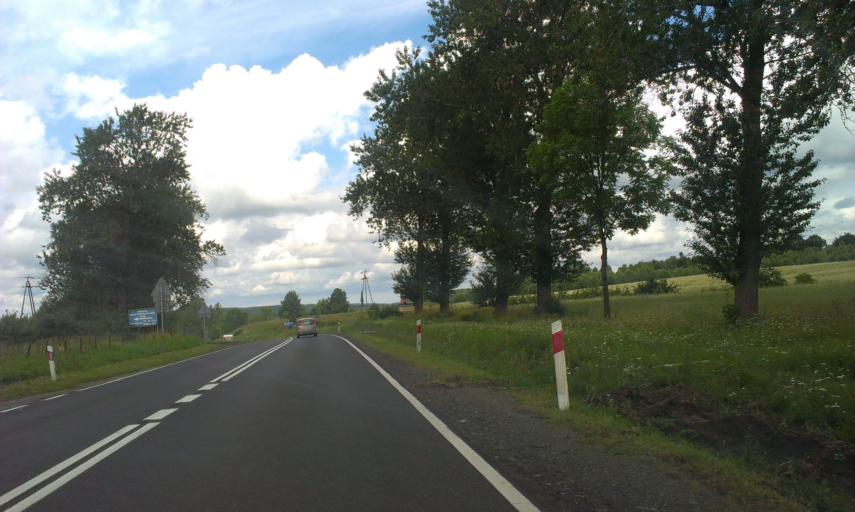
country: PL
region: West Pomeranian Voivodeship
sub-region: Powiat koszalinski
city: Bobolice
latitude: 53.9633
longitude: 16.5794
